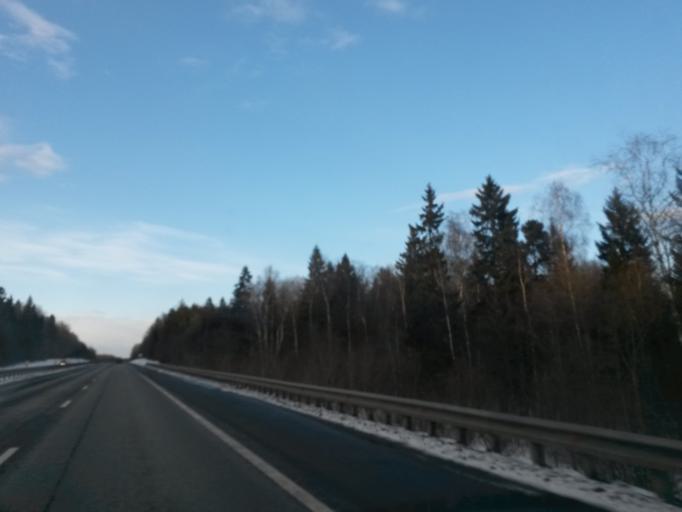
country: RU
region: Moskovskaya
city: Svatkovo
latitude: 56.3987
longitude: 38.3274
